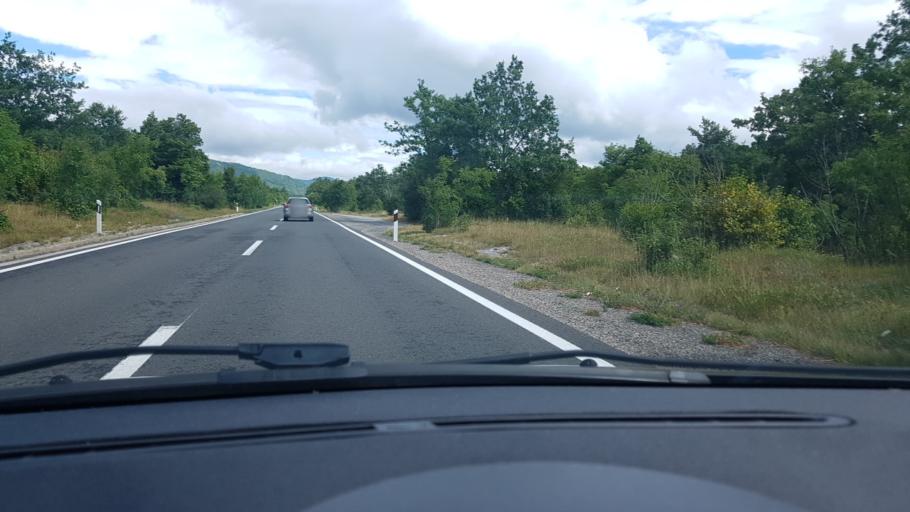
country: HR
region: Zadarska
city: Gracac
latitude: 44.4577
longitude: 15.8181
